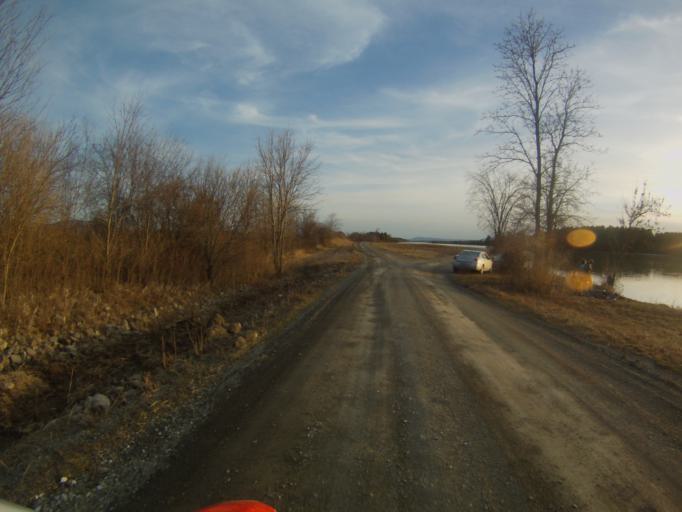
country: US
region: Vermont
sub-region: Addison County
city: Vergennes
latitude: 44.1259
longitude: -73.3289
